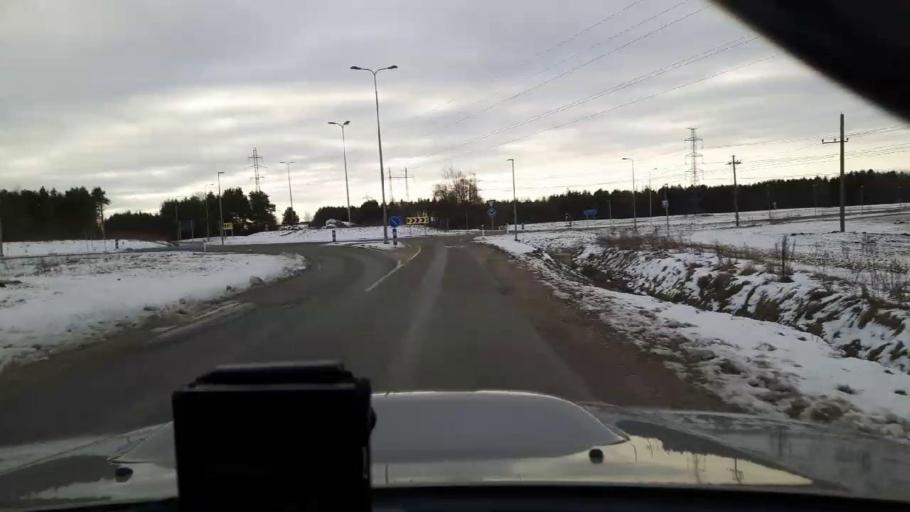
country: EE
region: Harju
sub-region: Saue vald
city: Laagri
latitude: 59.3474
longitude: 24.5995
